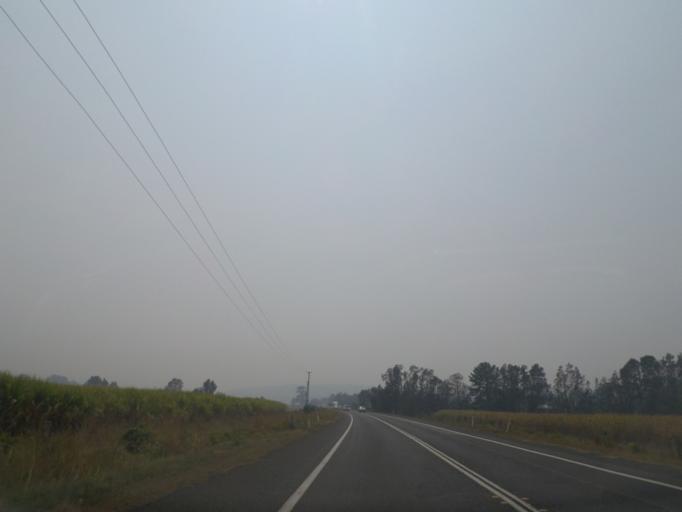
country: AU
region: New South Wales
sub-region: Clarence Valley
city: Maclean
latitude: -29.5670
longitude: 153.1342
